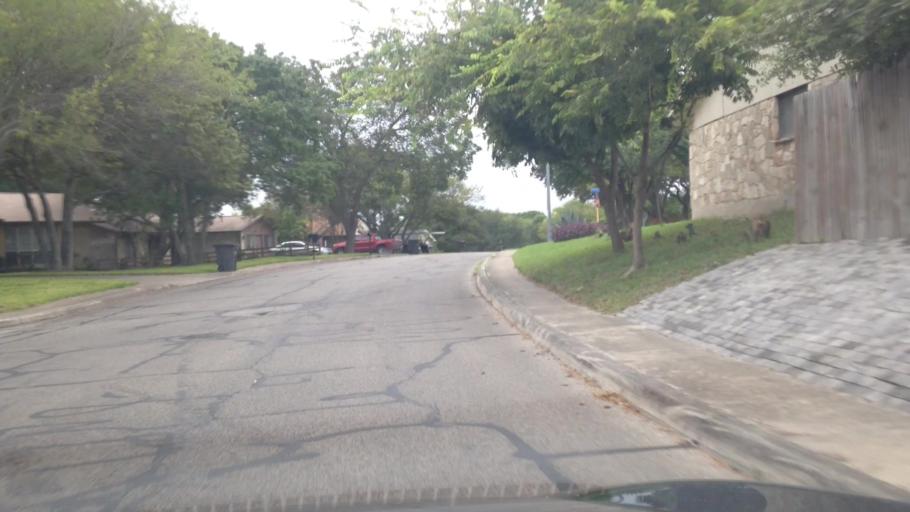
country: US
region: Texas
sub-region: Bexar County
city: Windcrest
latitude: 29.5733
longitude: -98.4130
